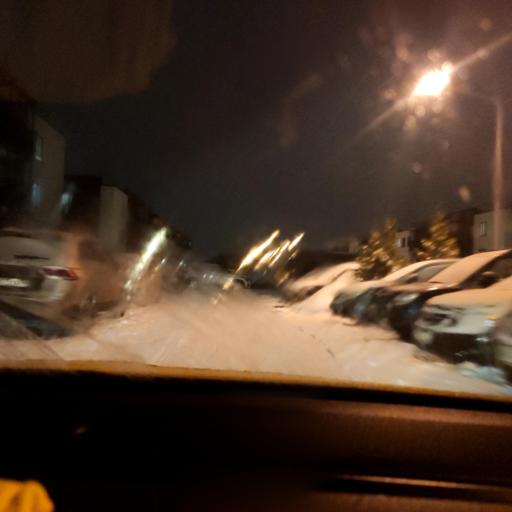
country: RU
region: Moskovskaya
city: Rozhdestveno
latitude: 55.8040
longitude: 36.9883
